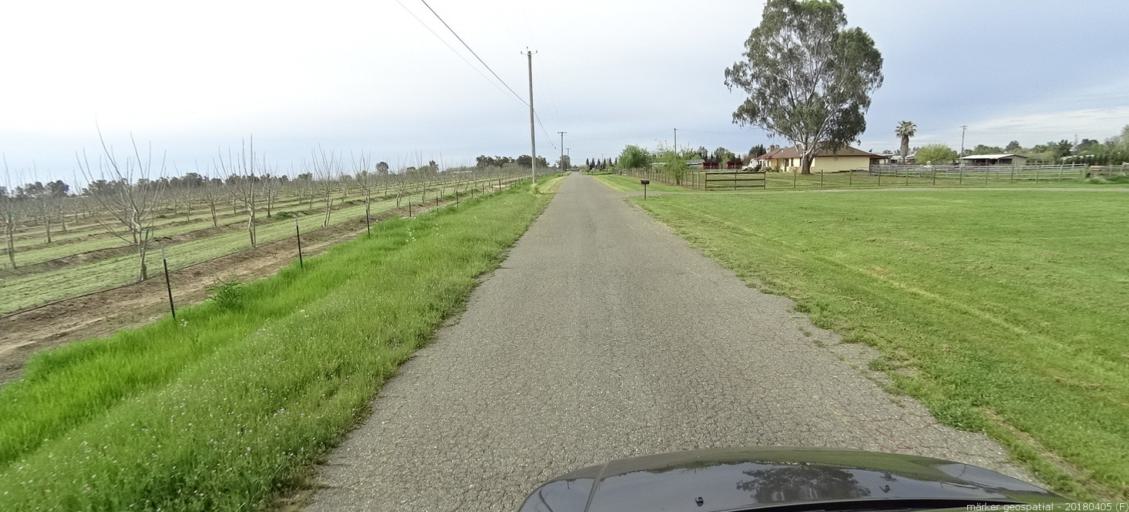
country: US
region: California
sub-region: Sacramento County
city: Herald
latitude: 38.2969
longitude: -121.2553
